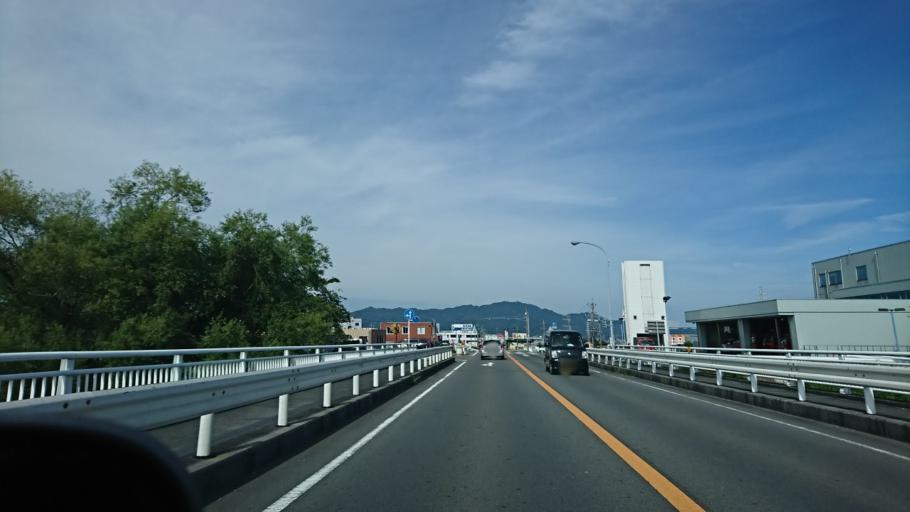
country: JP
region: Shizuoka
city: Fujieda
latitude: 34.8634
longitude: 138.2547
